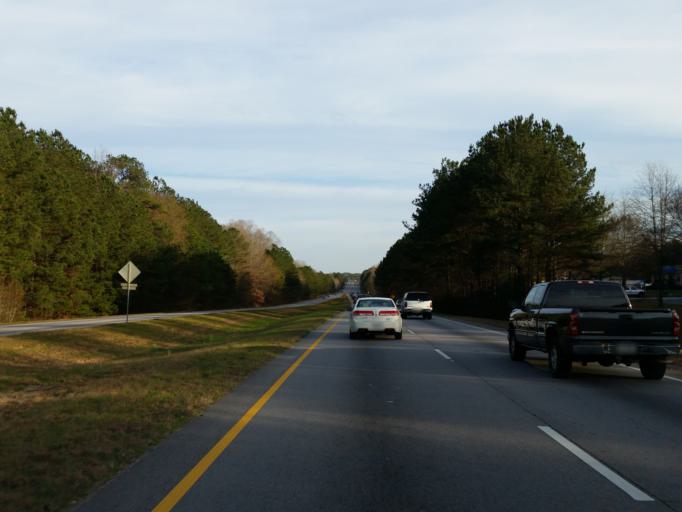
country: US
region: Georgia
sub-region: Cobb County
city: Powder Springs
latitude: 33.8793
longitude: -84.7172
